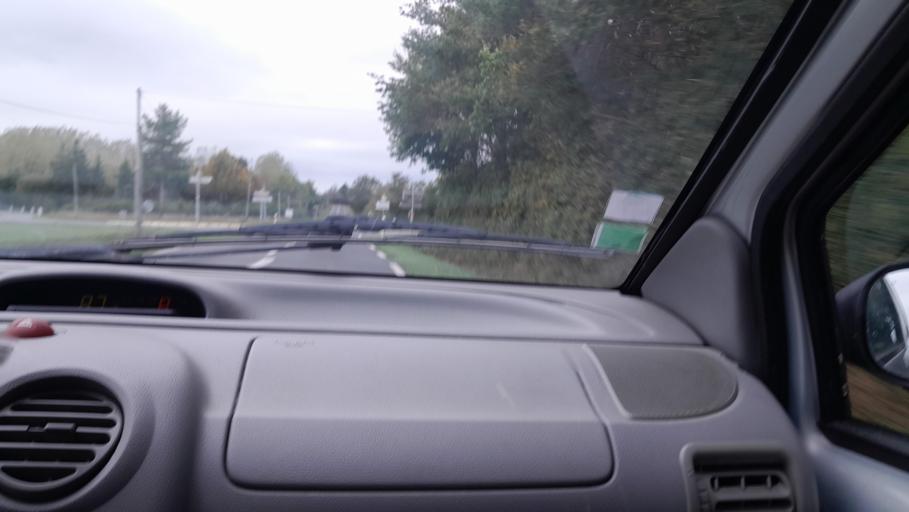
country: FR
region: Pays de la Loire
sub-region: Departement de la Loire-Atlantique
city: Saint-Mars-la-Jaille
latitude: 47.5975
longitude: -1.1980
